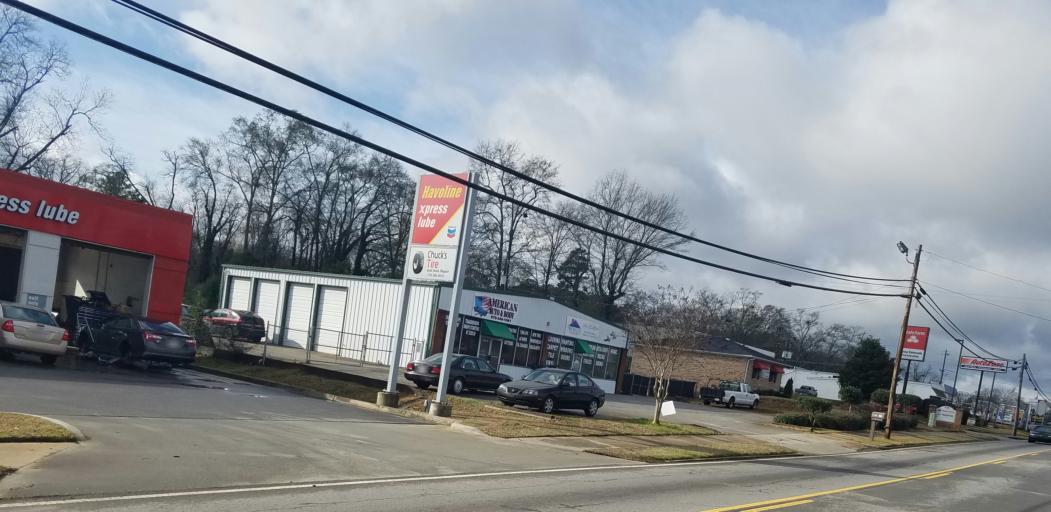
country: US
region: Georgia
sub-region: Butts County
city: Jackson
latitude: 33.2944
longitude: -83.9565
